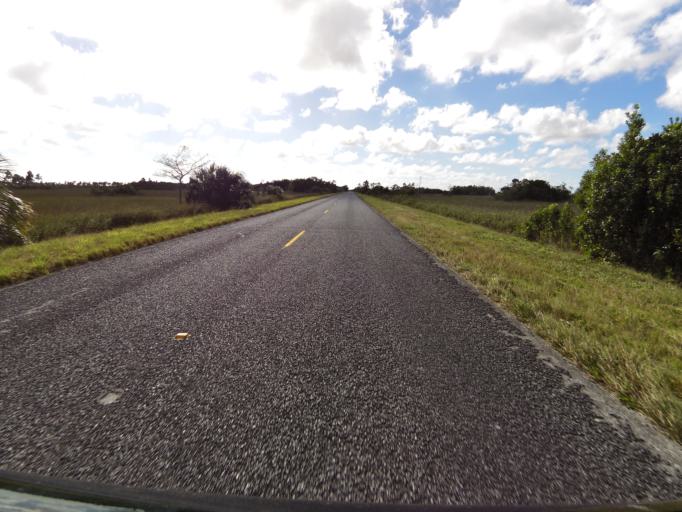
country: US
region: Florida
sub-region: Miami-Dade County
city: Florida City
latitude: 25.3975
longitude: -80.7958
